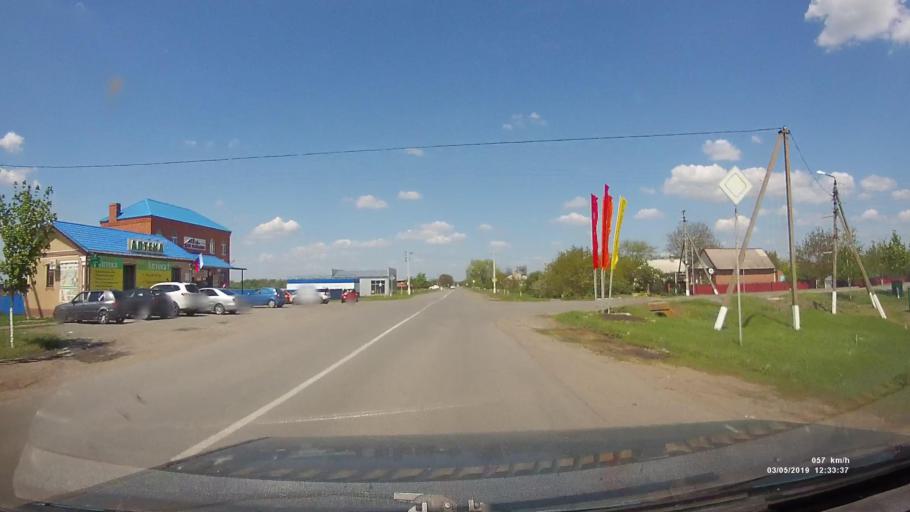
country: RU
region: Rostov
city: Semikarakorsk
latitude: 47.5142
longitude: 40.7715
